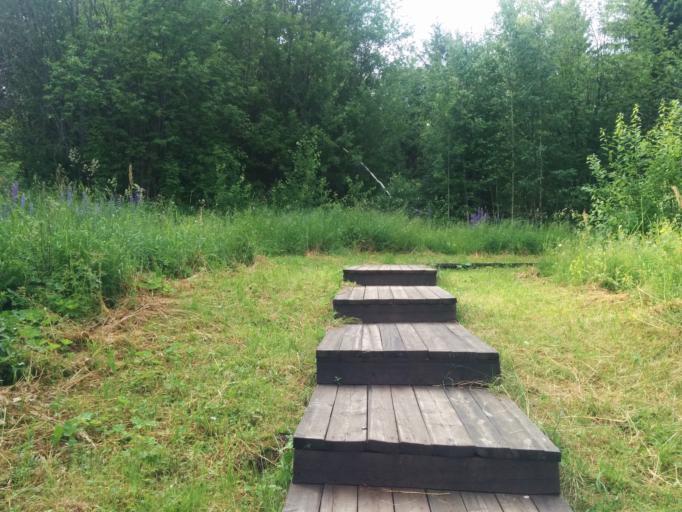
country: RU
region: Perm
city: Polazna
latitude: 58.2624
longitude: 56.2654
